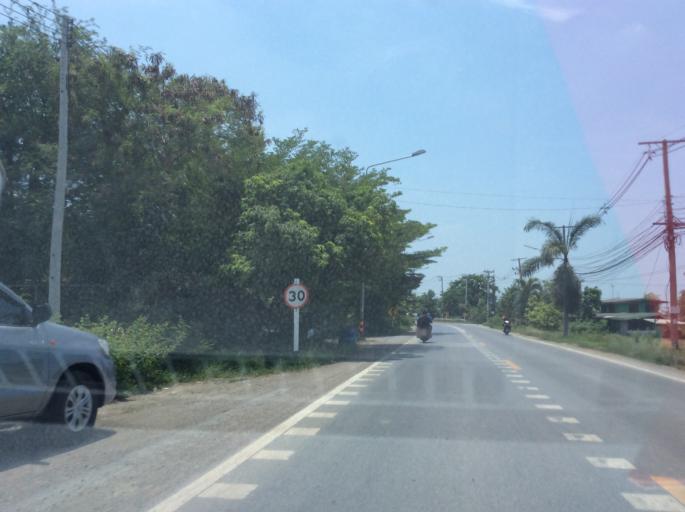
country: TH
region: Pathum Thani
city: Ban Rangsit
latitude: 14.0177
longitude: 100.7796
